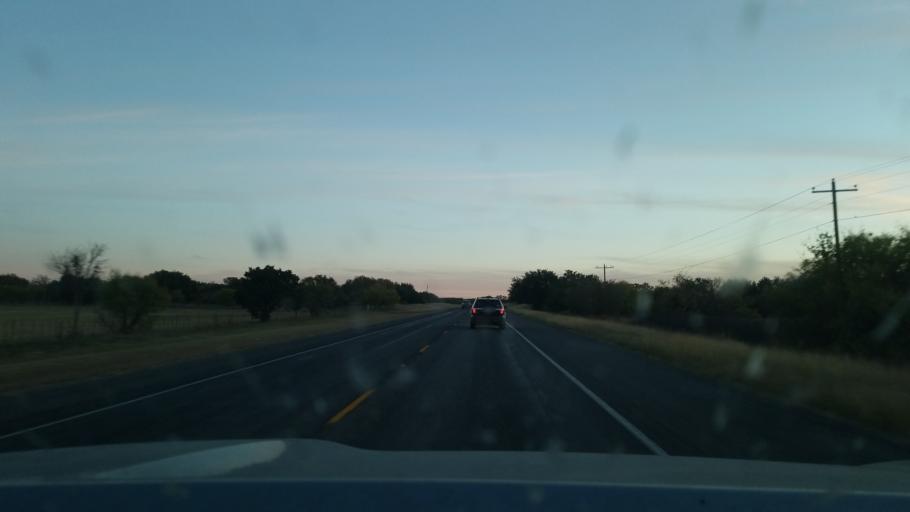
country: US
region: Texas
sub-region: Stephens County
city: Breckenridge
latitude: 32.5870
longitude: -98.8976
